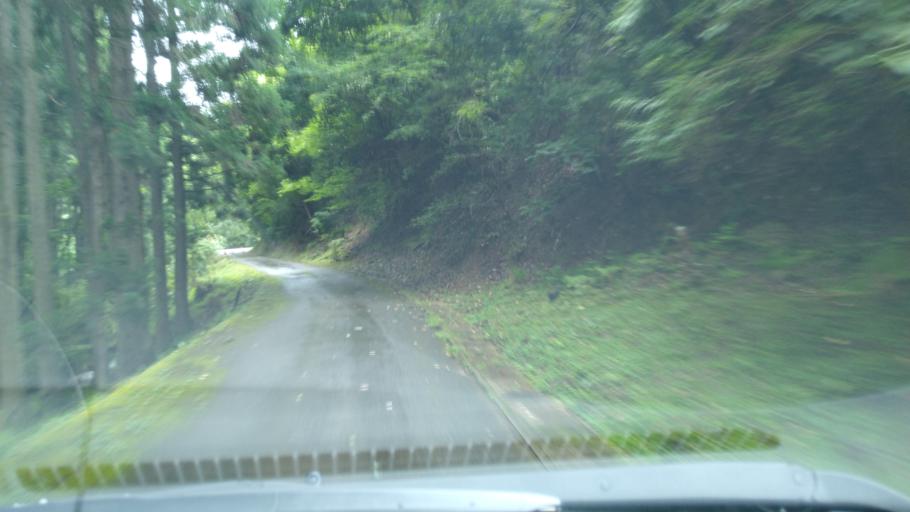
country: JP
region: Kyoto
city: Ayabe
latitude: 35.2363
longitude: 135.2669
